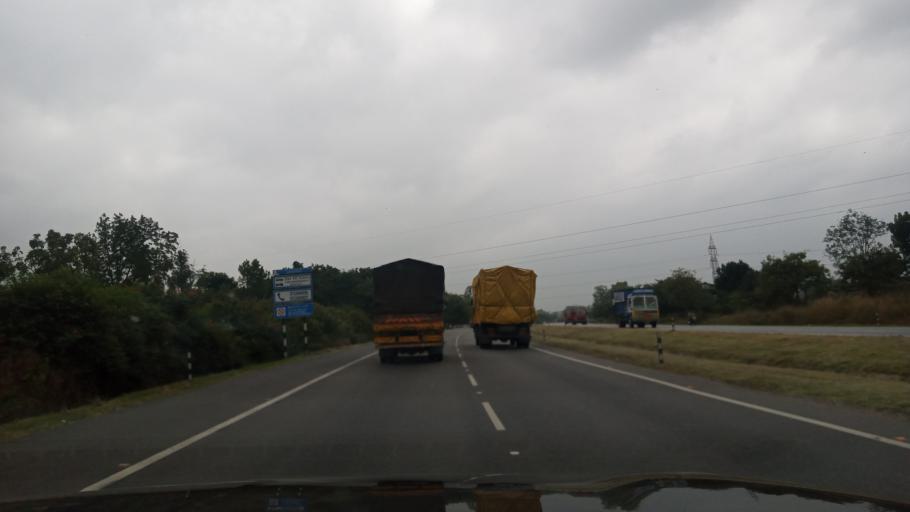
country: IN
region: Karnataka
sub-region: Bangalore Rural
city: Nelamangala
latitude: 13.0377
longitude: 77.4760
